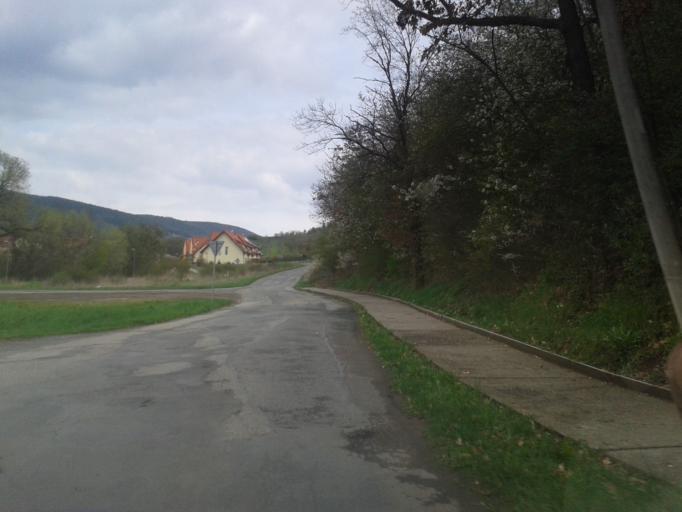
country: CZ
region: Central Bohemia
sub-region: Okres Beroun
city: Kraluv Dvur
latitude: 49.9513
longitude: 14.0287
